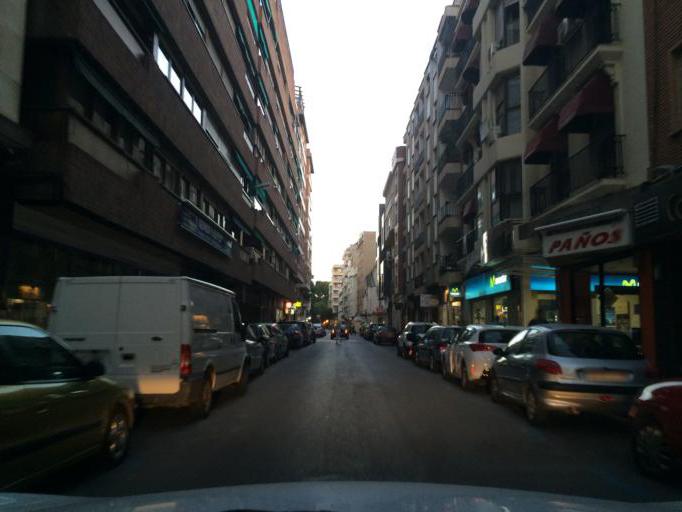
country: ES
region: Castille-La Mancha
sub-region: Provincia de Albacete
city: Albacete
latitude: 38.9922
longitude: -1.8547
